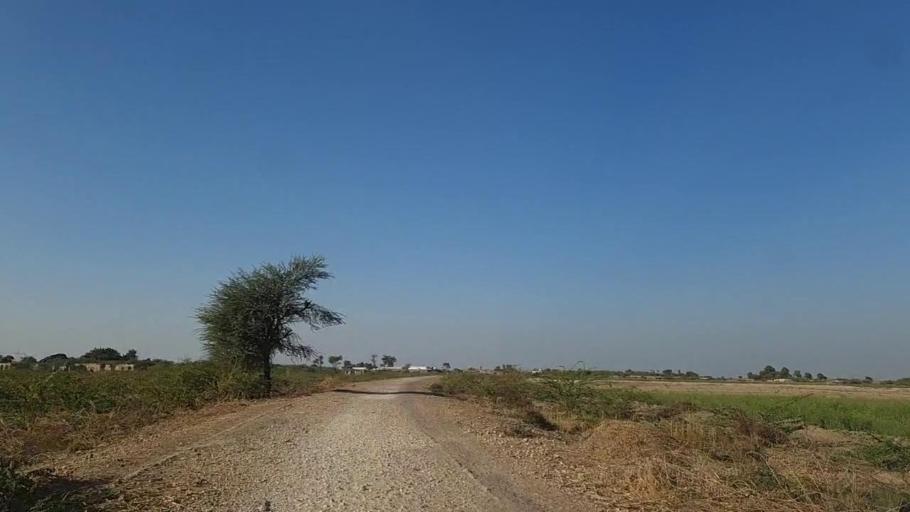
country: PK
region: Sindh
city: Samaro
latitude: 25.3593
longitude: 69.3755
